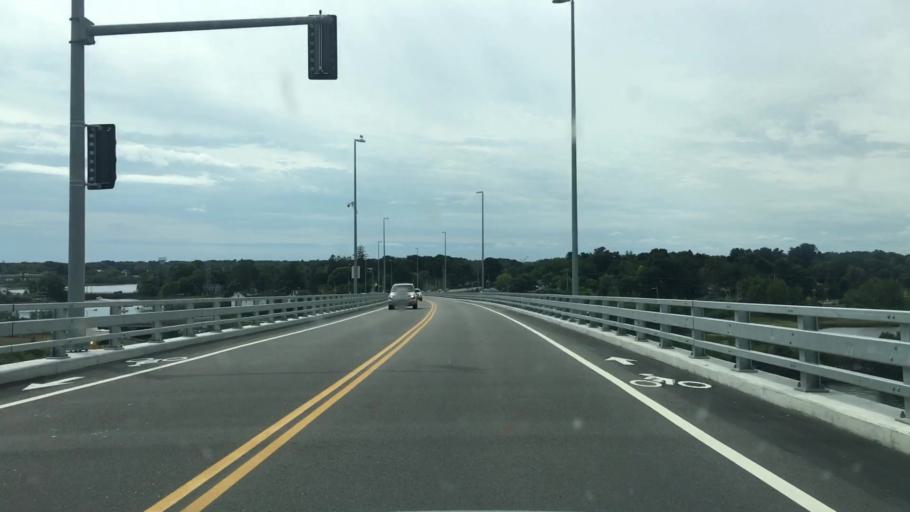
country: US
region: New Hampshire
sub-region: Rockingham County
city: Portsmouth
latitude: 43.0859
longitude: -70.7622
